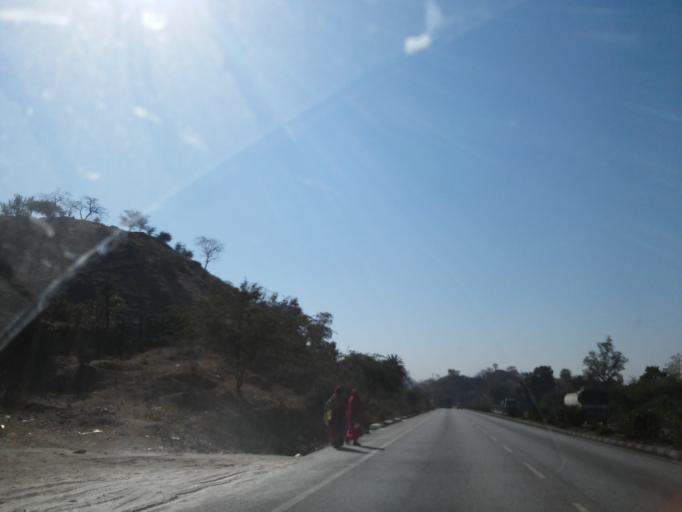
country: IN
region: Rajasthan
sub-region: Udaipur
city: Udaipur
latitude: 24.3052
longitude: 73.6778
